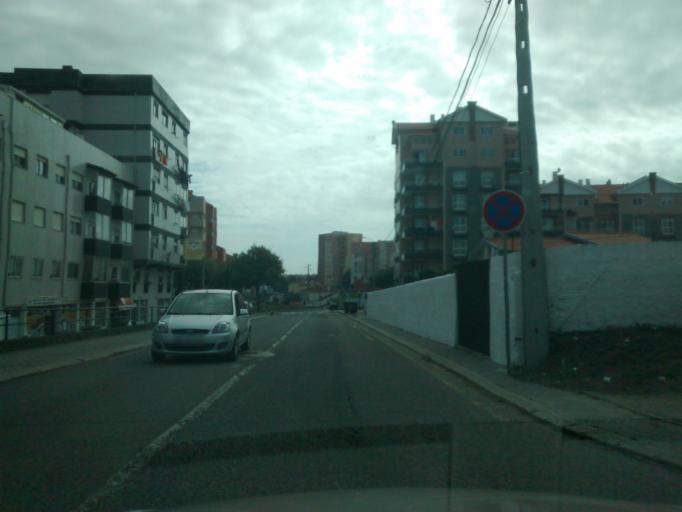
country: PT
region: Aveiro
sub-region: Aveiro
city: Aveiro
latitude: 40.6549
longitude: -8.6225
